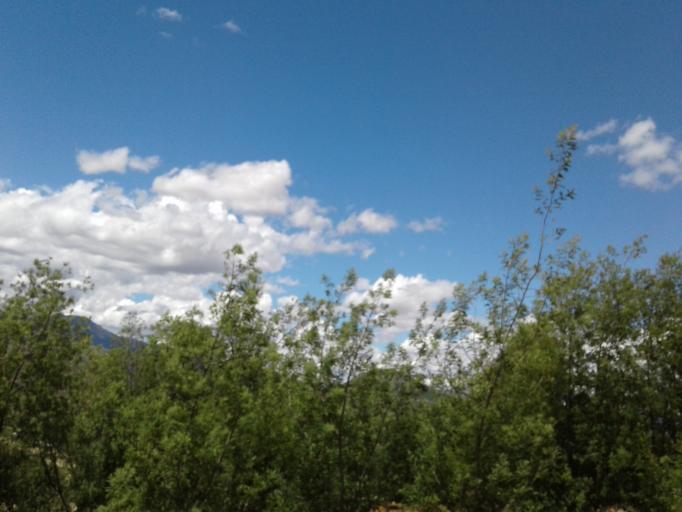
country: LS
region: Quthing
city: Quthing
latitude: -30.3857
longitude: 27.5574
